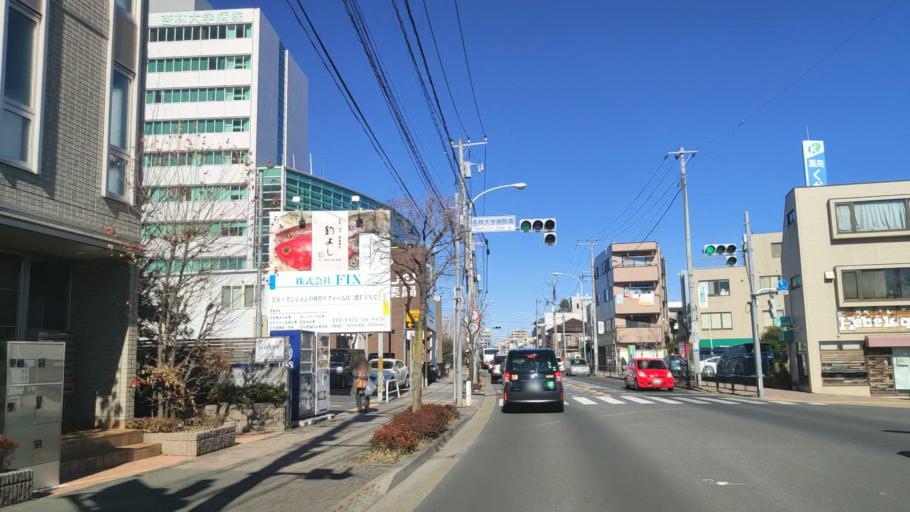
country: JP
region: Tokyo
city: Mitaka-shi
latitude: 35.6767
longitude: 139.5678
